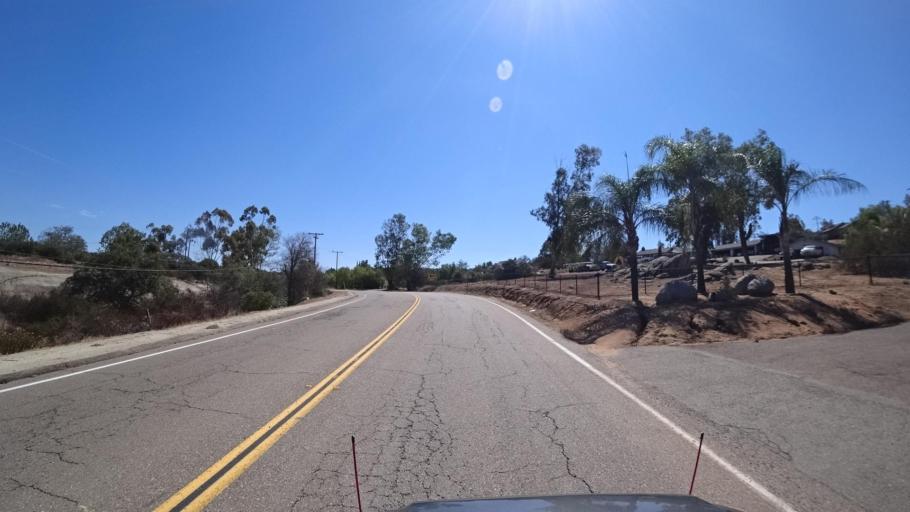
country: US
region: California
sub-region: San Diego County
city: Ramona
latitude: 33.0381
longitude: -116.8349
